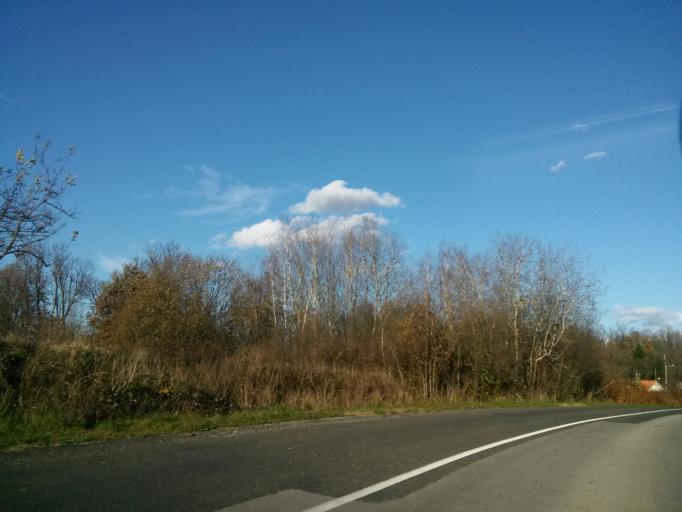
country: HR
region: Sisacko-Moslavacka
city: Gvozd
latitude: 45.3909
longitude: 15.9159
